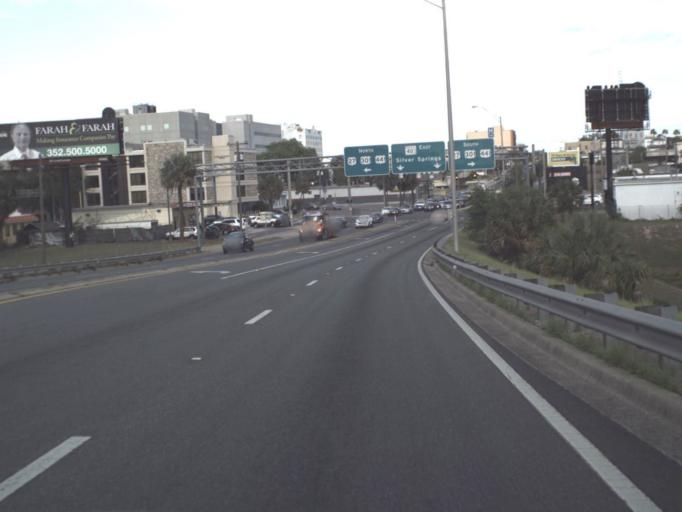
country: US
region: Florida
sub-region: Marion County
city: Ocala
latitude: 29.1869
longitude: -82.1420
